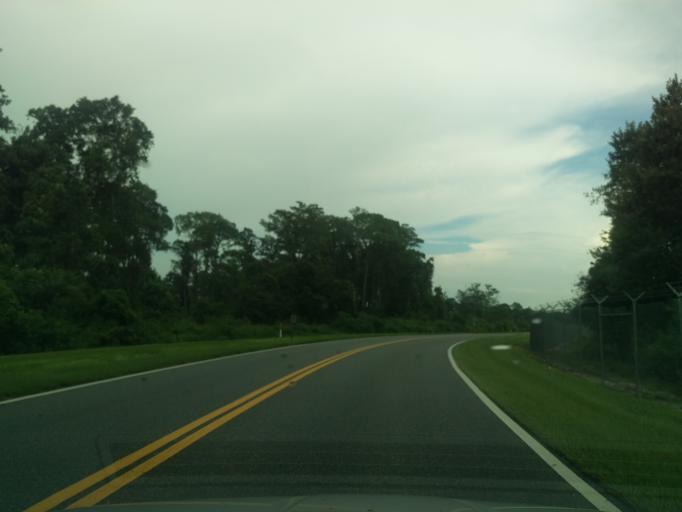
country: US
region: Florida
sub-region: Orange County
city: Bay Hill
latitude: 28.4237
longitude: -81.5855
